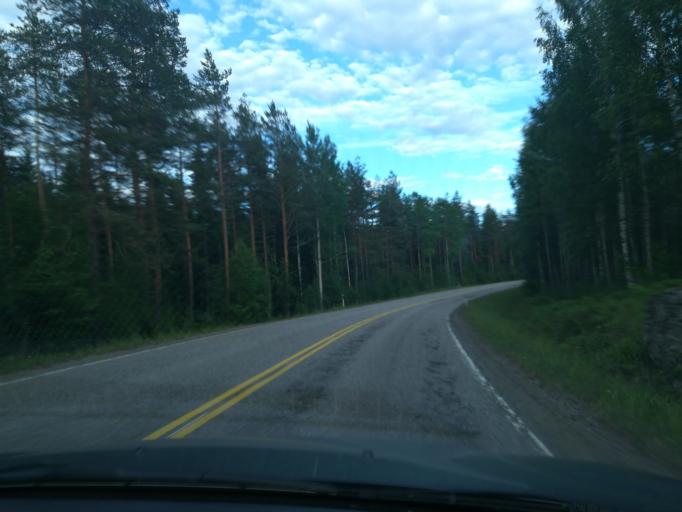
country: FI
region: Southern Savonia
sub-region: Mikkeli
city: Puumala
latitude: 61.5190
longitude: 27.8985
